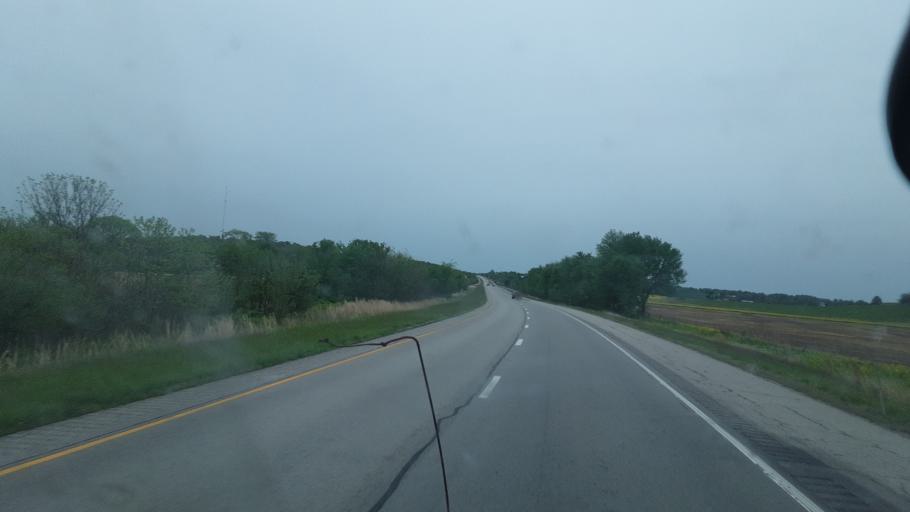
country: US
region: Indiana
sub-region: Dubois County
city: Ferdinand
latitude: 38.1995
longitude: -86.9152
